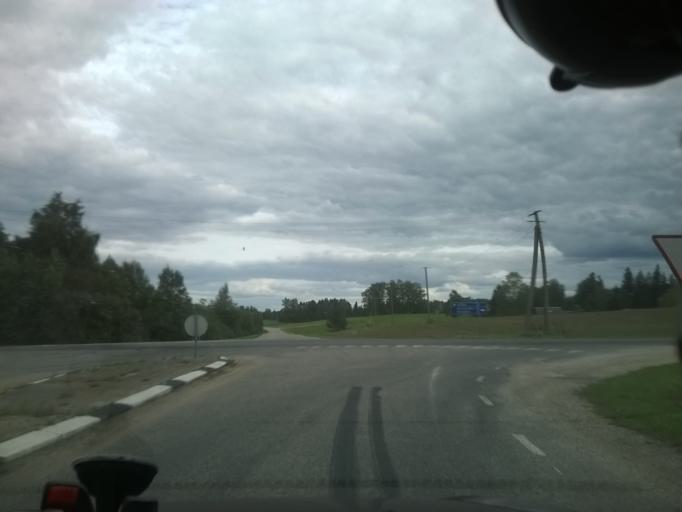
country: EE
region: Vorumaa
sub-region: Voru linn
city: Voru
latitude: 57.7835
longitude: 27.0345
